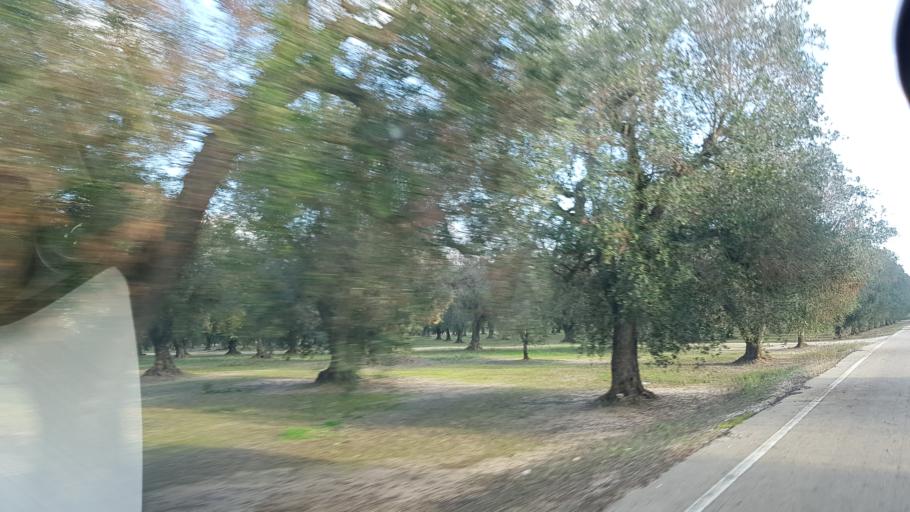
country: IT
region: Apulia
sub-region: Provincia di Brindisi
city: San Pietro Vernotico
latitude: 40.5129
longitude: 18.0162
